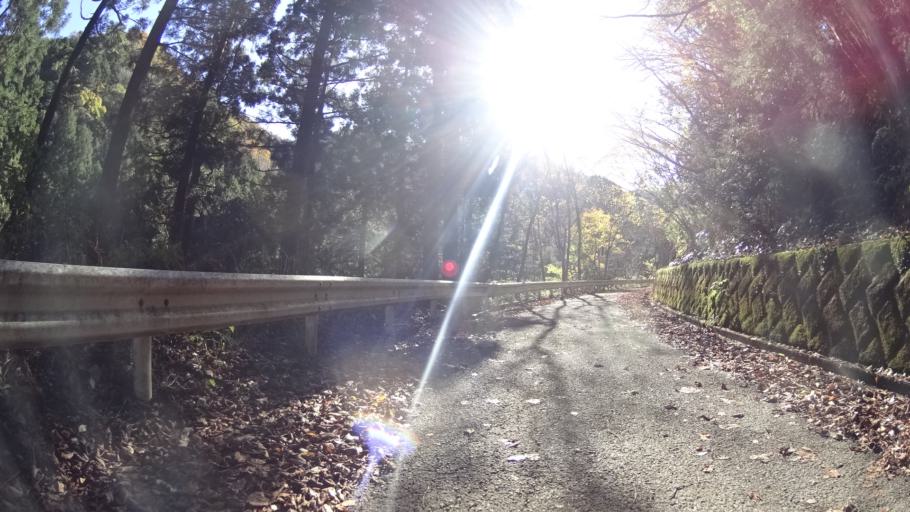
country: JP
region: Kanagawa
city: Atsugi
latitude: 35.5161
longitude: 139.2733
